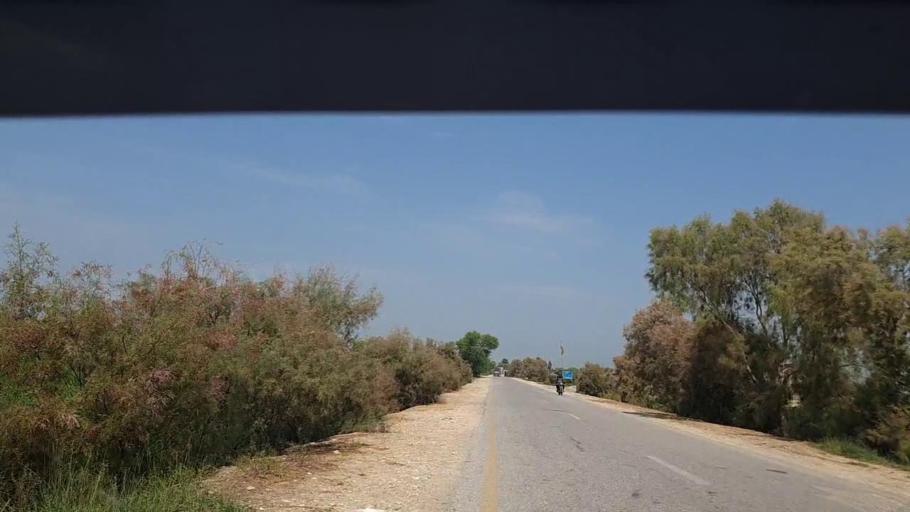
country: PK
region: Sindh
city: Thul
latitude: 28.1456
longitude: 68.8176
